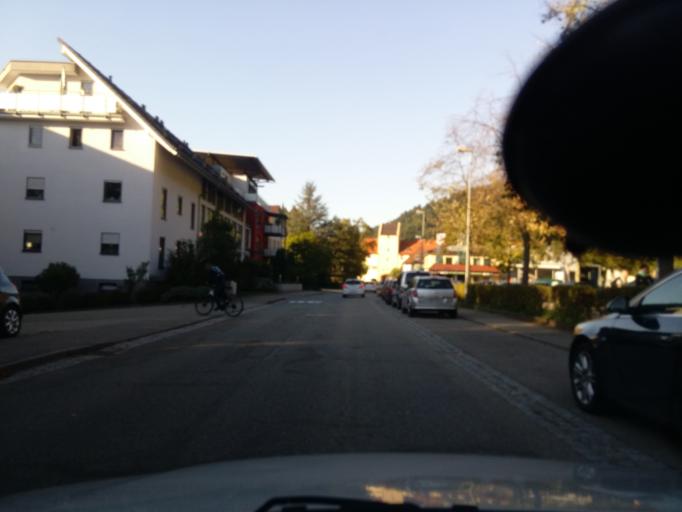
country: DE
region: Baden-Wuerttemberg
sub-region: Freiburg Region
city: Wolfach
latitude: 48.2958
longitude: 8.2214
